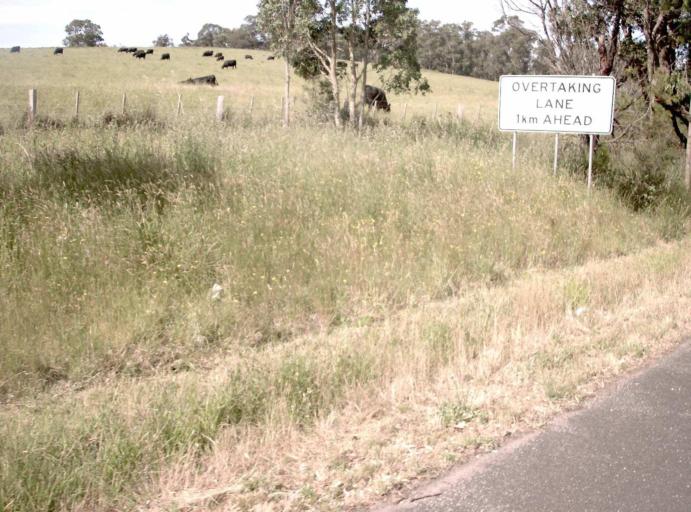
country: AU
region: Victoria
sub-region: East Gippsland
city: Lakes Entrance
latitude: -37.8243
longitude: 147.8817
